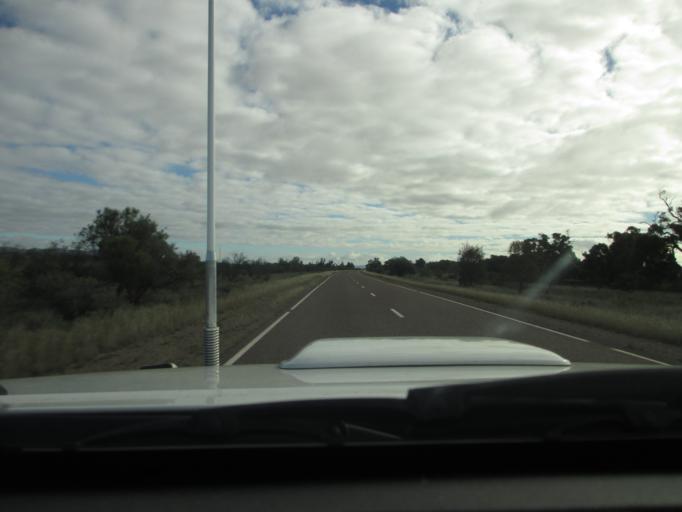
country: AU
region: South Australia
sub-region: Flinders Ranges
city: Quorn
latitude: -32.4846
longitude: 138.5443
